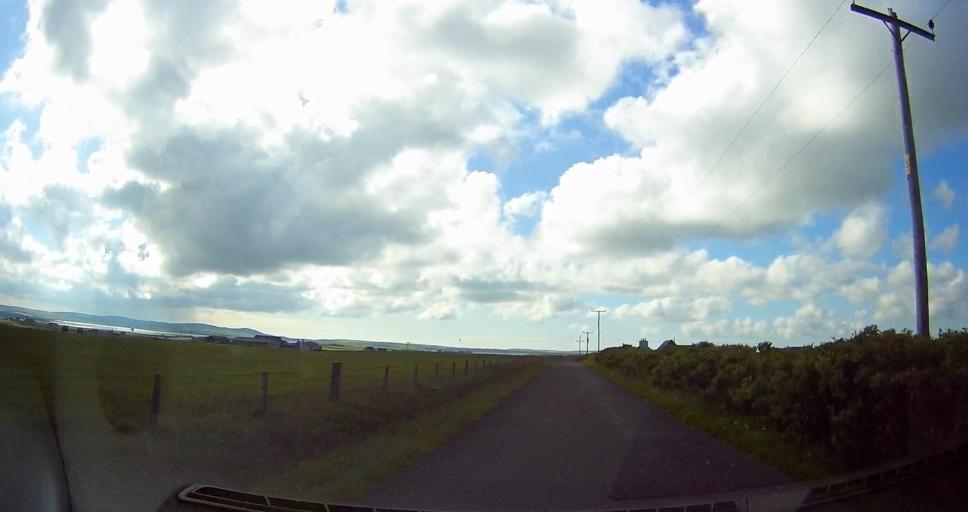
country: GB
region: Scotland
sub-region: Orkney Islands
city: Stromness
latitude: 58.9955
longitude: -3.1607
